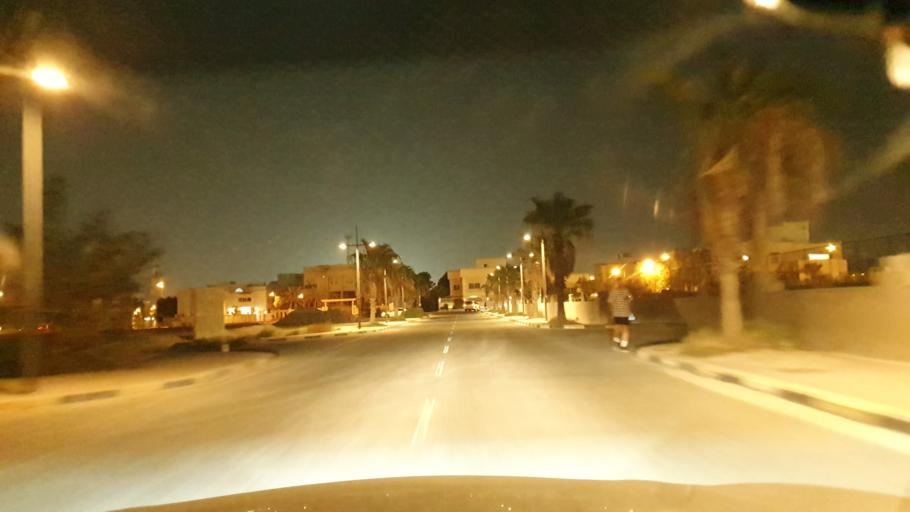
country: BH
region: Northern
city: Madinat `Isa
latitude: 26.1554
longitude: 50.5472
